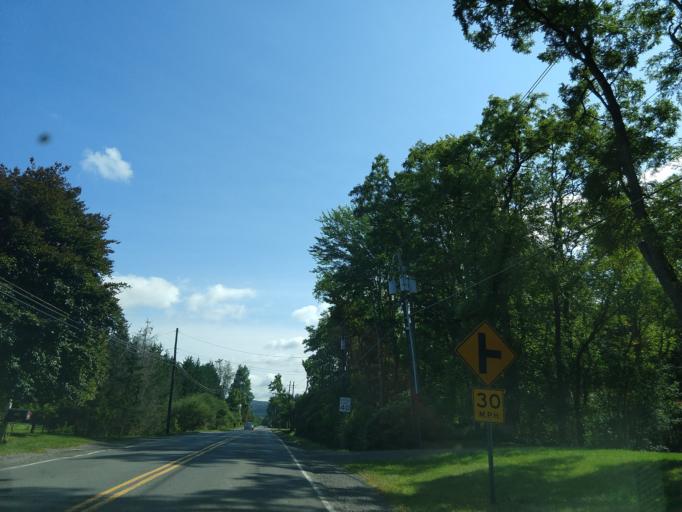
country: US
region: New York
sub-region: Tompkins County
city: South Hill
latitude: 42.4170
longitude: -76.4795
